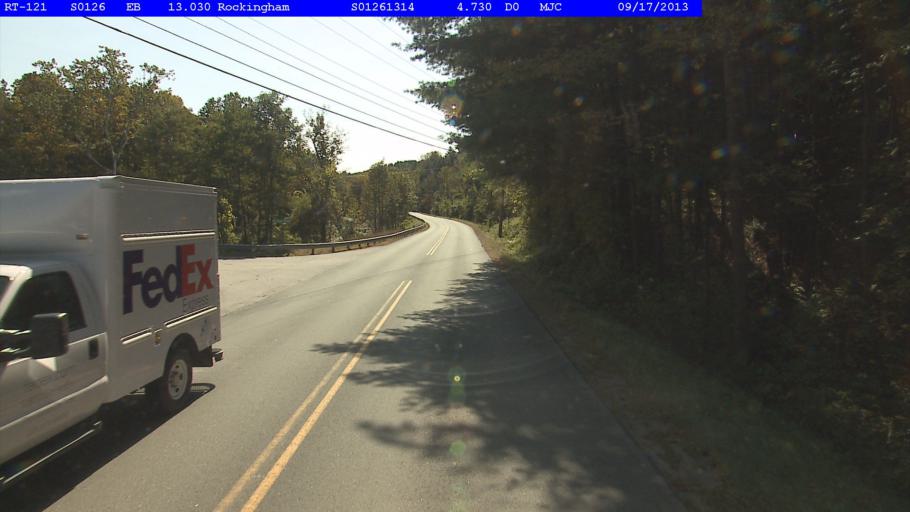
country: US
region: Vermont
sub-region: Windham County
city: Bellows Falls
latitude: 43.1315
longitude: -72.4818
